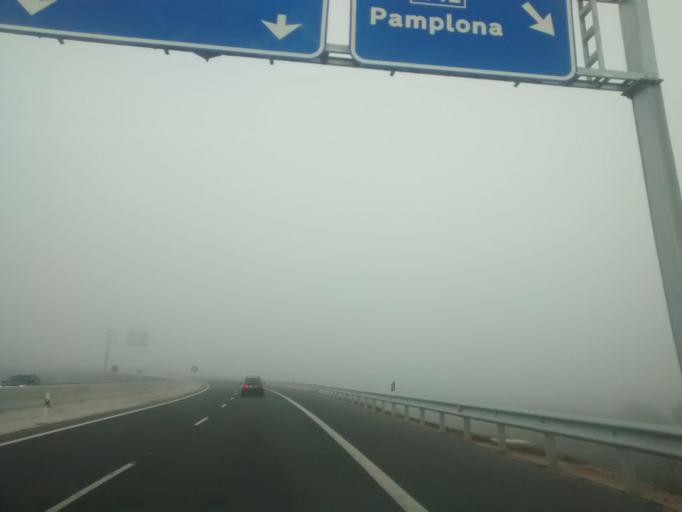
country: ES
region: Navarre
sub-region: Provincia de Navarra
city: Viana
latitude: 42.4567
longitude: -2.3620
